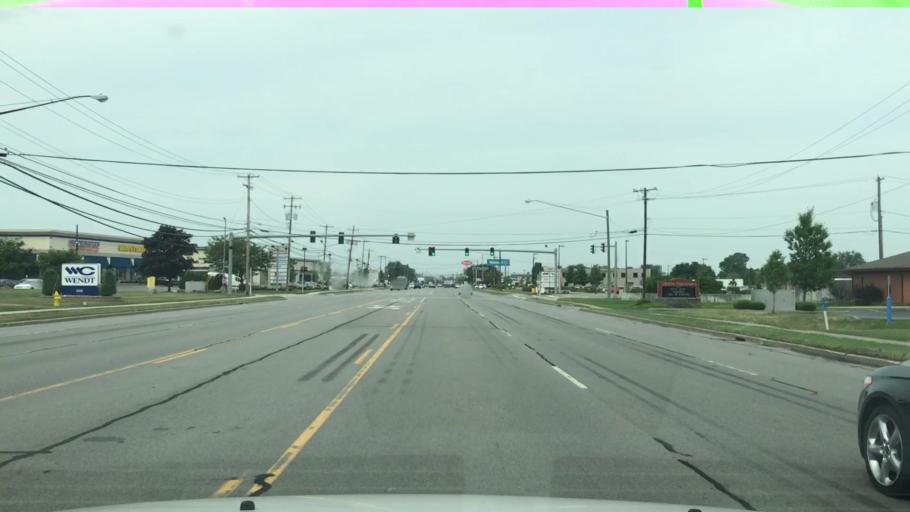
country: US
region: New York
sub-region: Erie County
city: Cheektowaga
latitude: 42.9086
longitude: -78.7409
